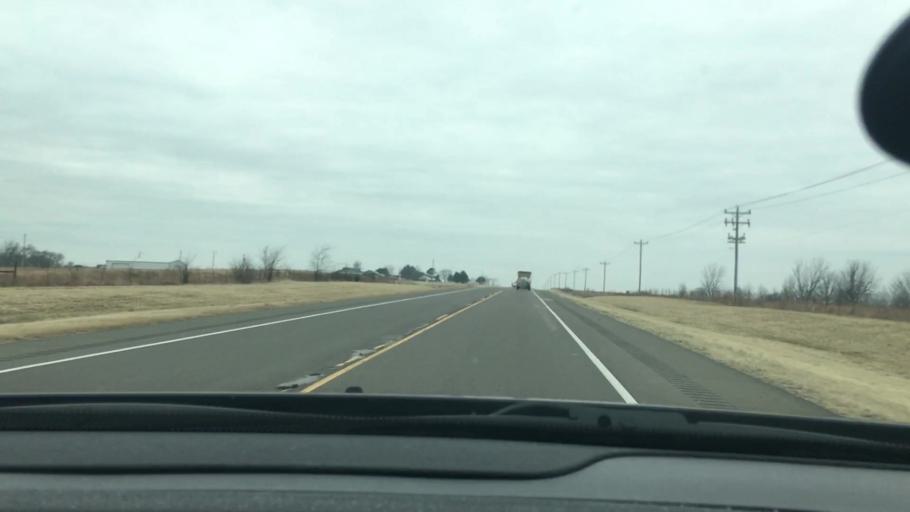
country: US
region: Oklahoma
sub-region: Murray County
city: Davis
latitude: 34.5213
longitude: -97.2202
